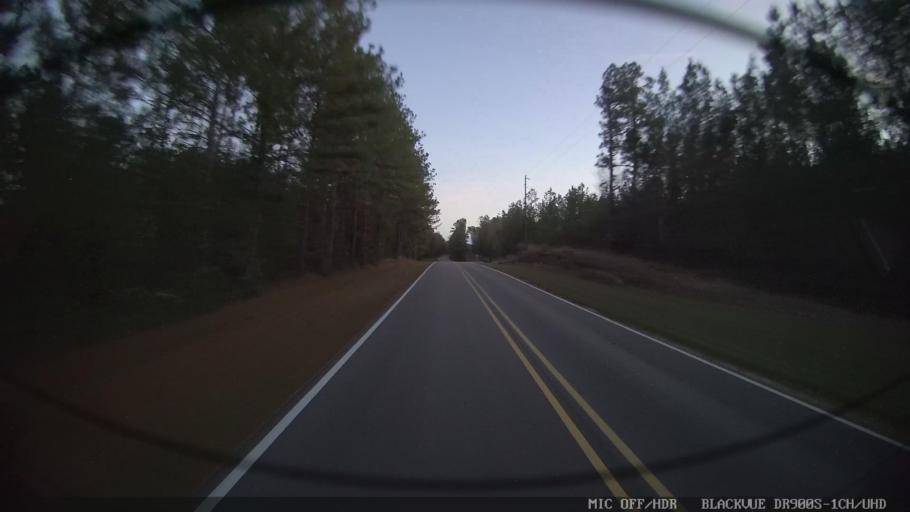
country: US
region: Mississippi
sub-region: Perry County
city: New Augusta
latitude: 31.0803
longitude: -89.1873
